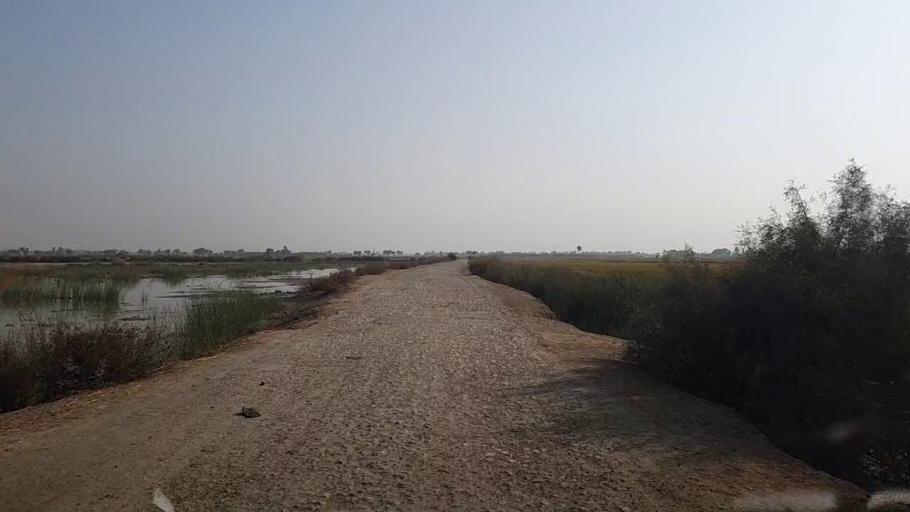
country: PK
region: Sindh
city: Kandhkot
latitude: 28.2920
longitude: 69.2533
